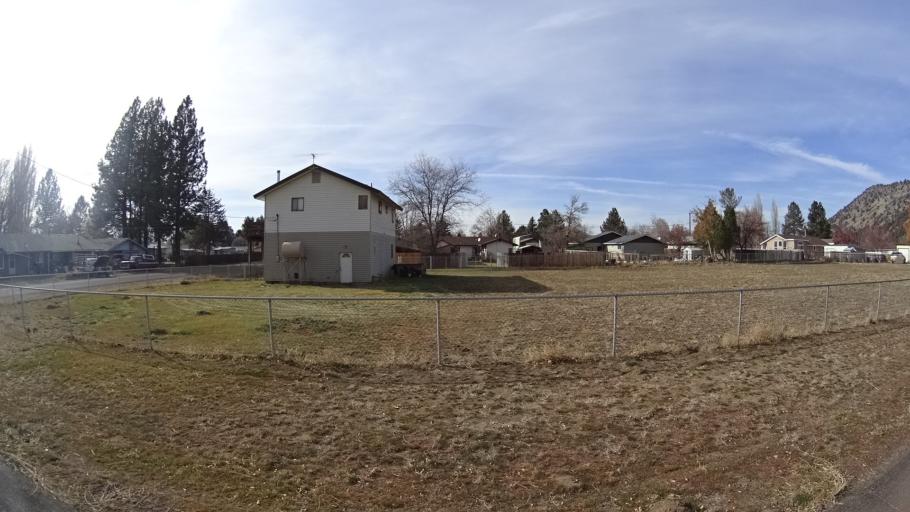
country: US
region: Oregon
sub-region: Klamath County
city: Klamath Falls
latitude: 41.9705
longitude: -121.9145
